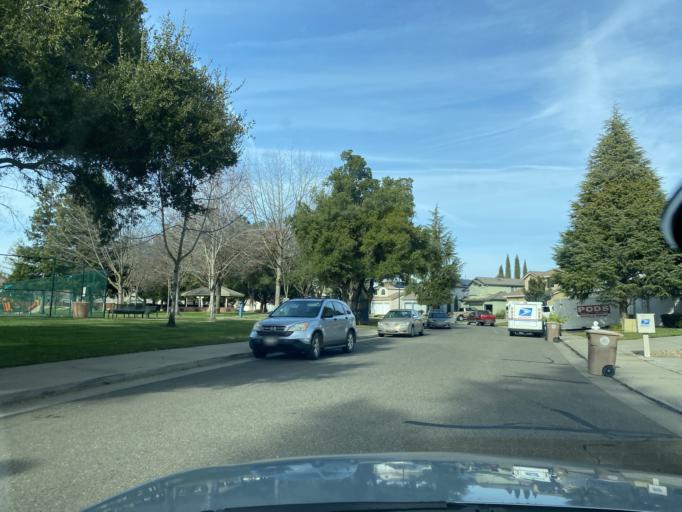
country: US
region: California
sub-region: Sacramento County
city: Elk Grove
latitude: 38.4336
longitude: -121.3766
